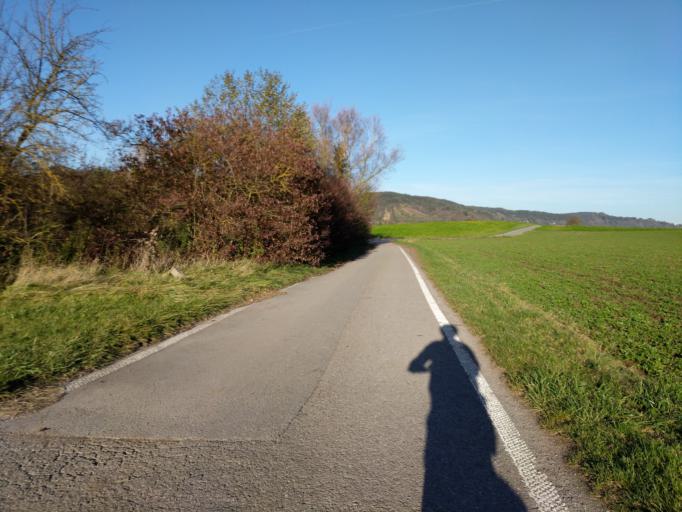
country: DE
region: Baden-Wuerttemberg
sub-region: Tuebingen Region
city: Rottenburg
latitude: 48.5140
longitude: 8.9801
